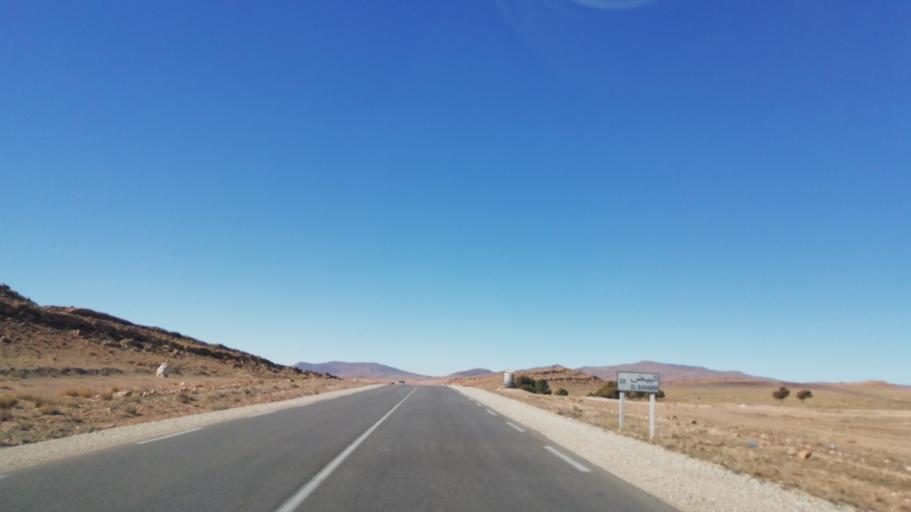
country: DZ
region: El Bayadh
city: El Bayadh
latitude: 33.6103
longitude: 1.2328
